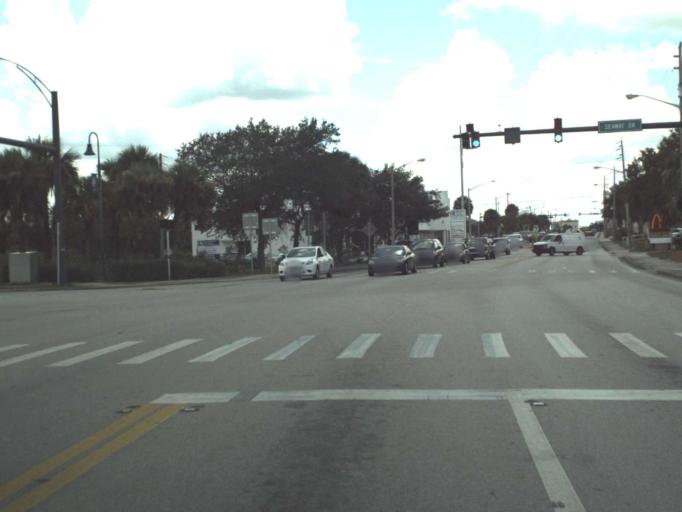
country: US
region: Florida
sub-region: Saint Lucie County
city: Fort Pierce
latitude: 27.4554
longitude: -80.3273
